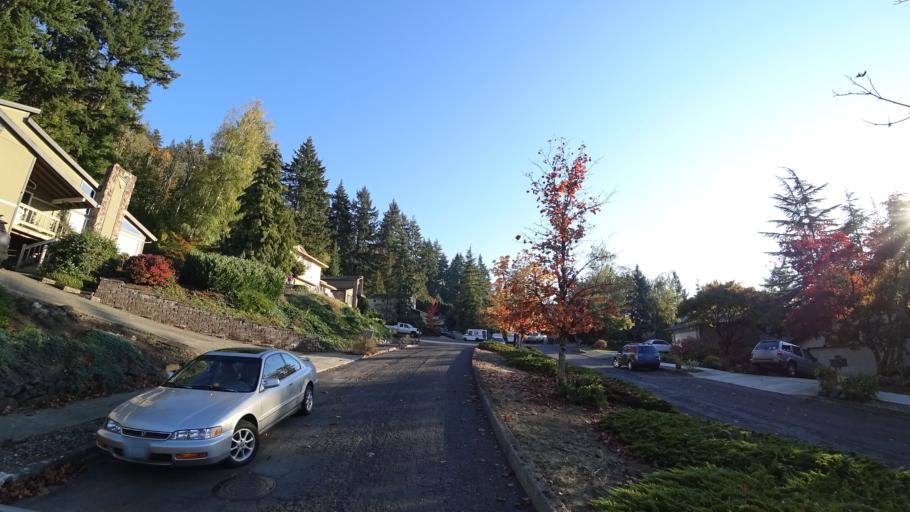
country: US
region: Oregon
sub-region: Multnomah County
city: Gresham
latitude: 45.4886
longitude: -122.4440
